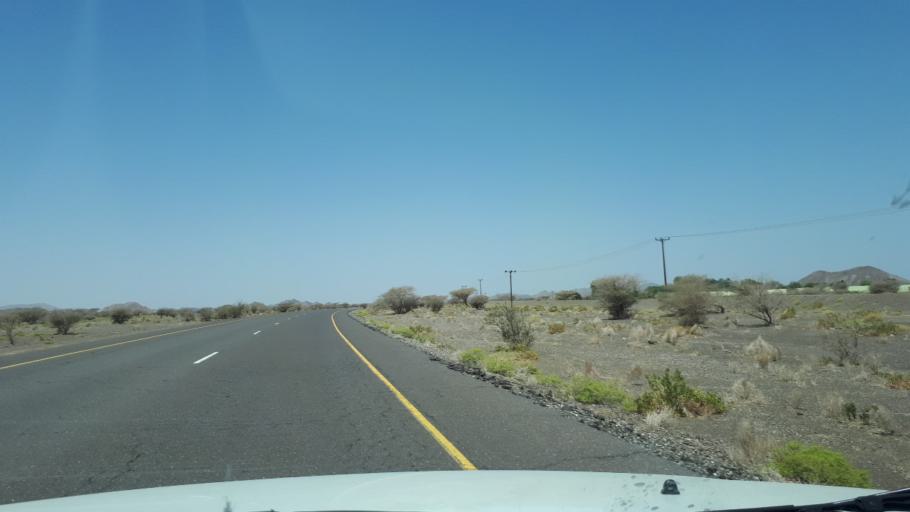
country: OM
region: Ash Sharqiyah
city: Ibra'
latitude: 22.6170
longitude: 58.4260
